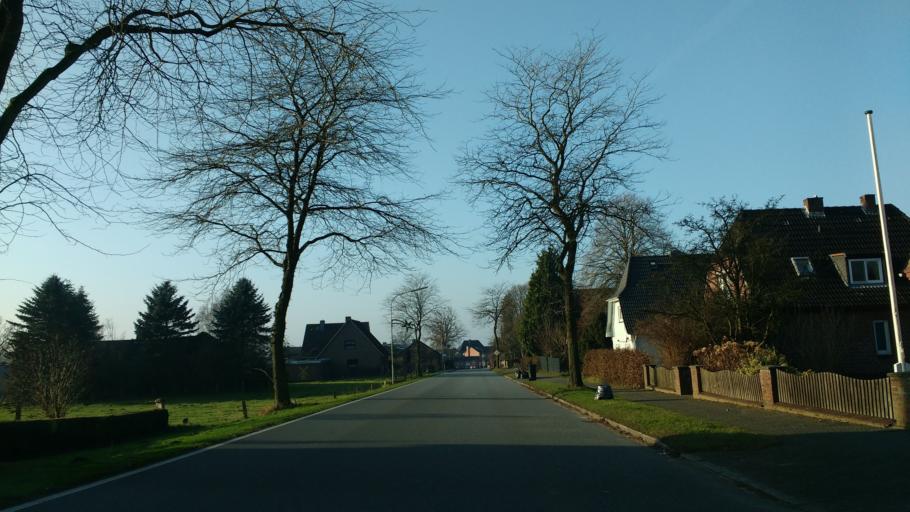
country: DE
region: Schleswig-Holstein
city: Wacken
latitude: 54.0203
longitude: 9.3804
